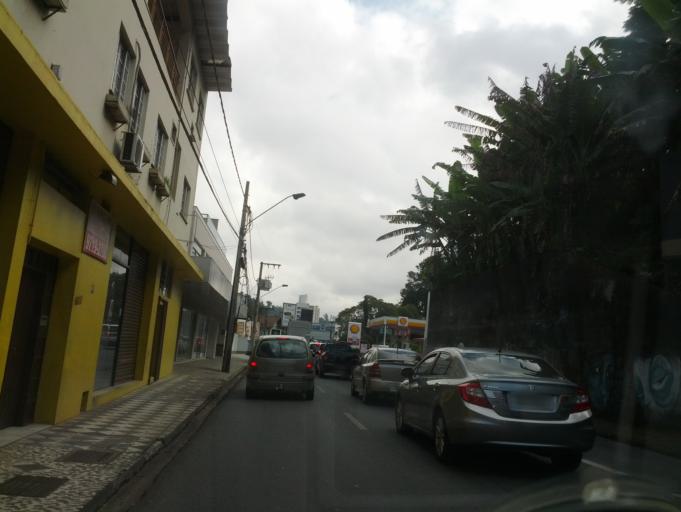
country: BR
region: Santa Catarina
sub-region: Blumenau
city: Blumenau
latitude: -26.9060
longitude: -49.0749
